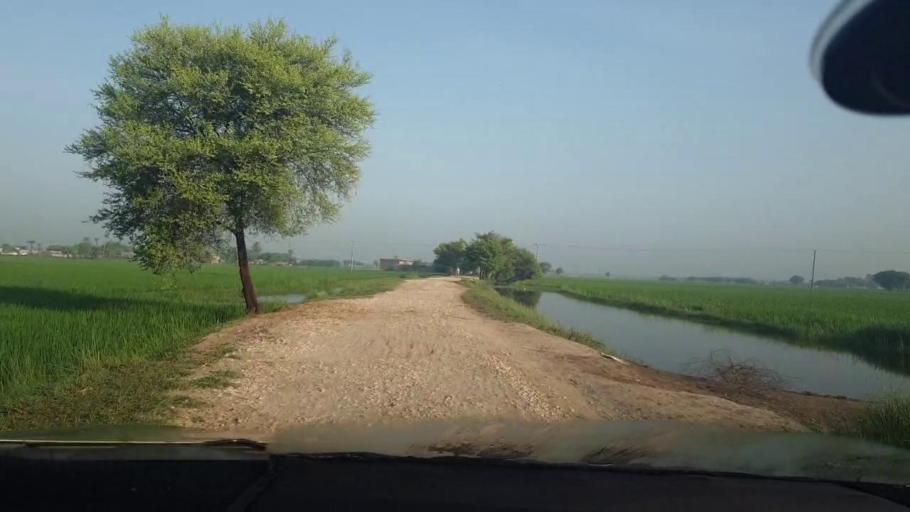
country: PK
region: Sindh
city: Kambar
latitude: 27.6282
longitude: 68.0185
